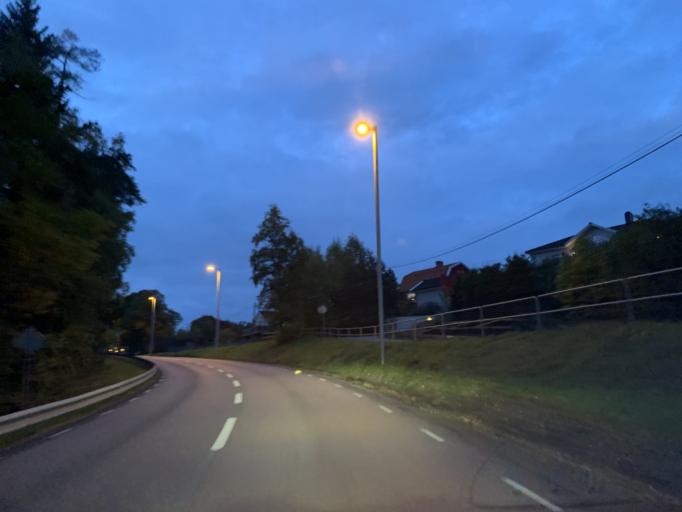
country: SE
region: Stockholm
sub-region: Botkyrka Kommun
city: Varsta
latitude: 59.1666
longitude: 17.7981
